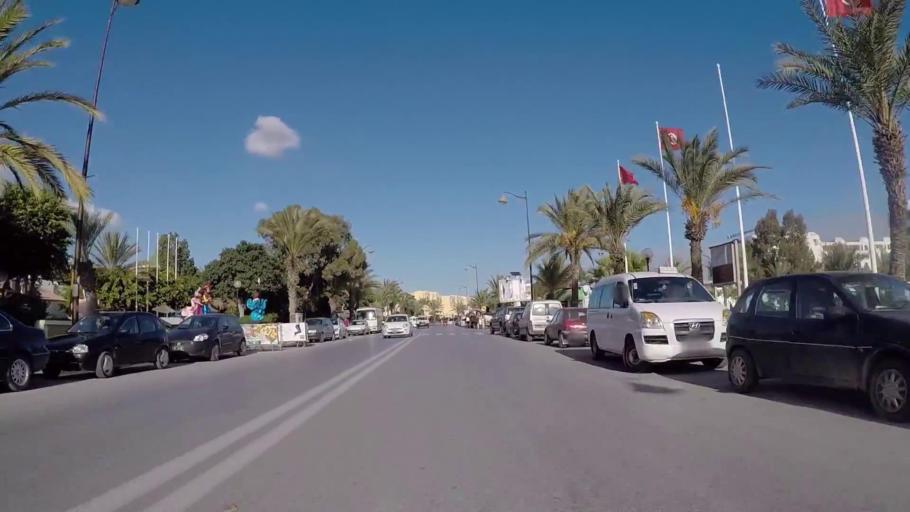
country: TN
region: Nabul
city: Al Hammamat
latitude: 36.3666
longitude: 10.5343
